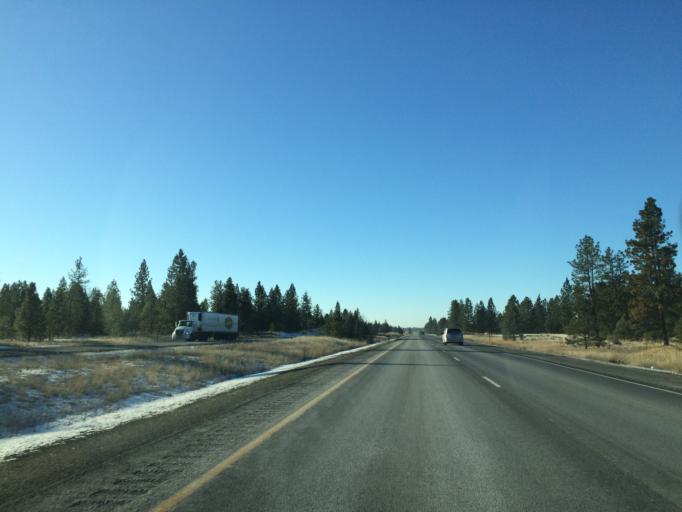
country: US
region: Washington
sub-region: Spokane County
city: Medical Lake
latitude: 47.4564
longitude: -117.7617
